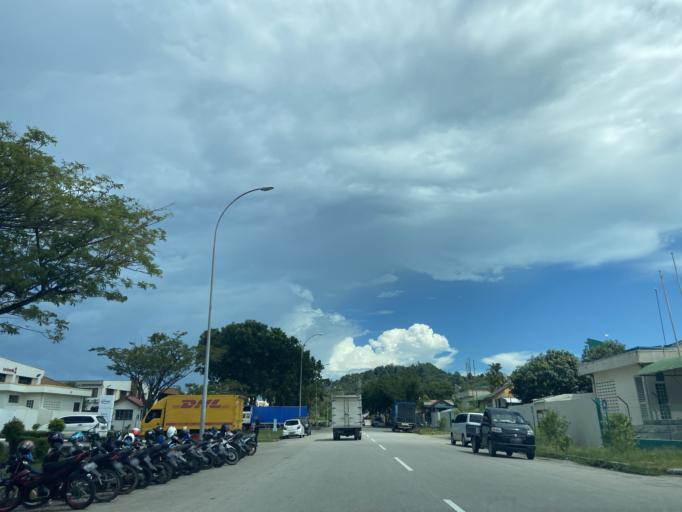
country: SG
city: Singapore
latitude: 1.0580
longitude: 104.0371
